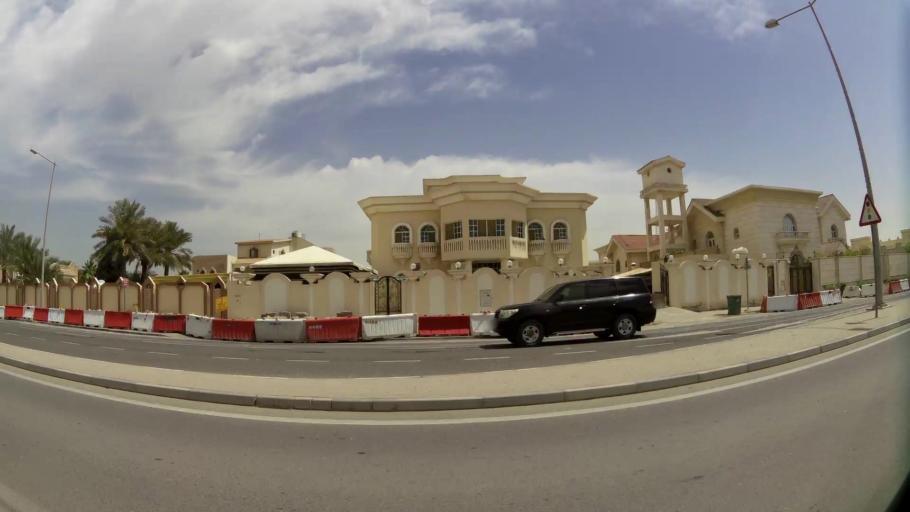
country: QA
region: Baladiyat ar Rayyan
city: Ar Rayyan
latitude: 25.2695
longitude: 51.4202
